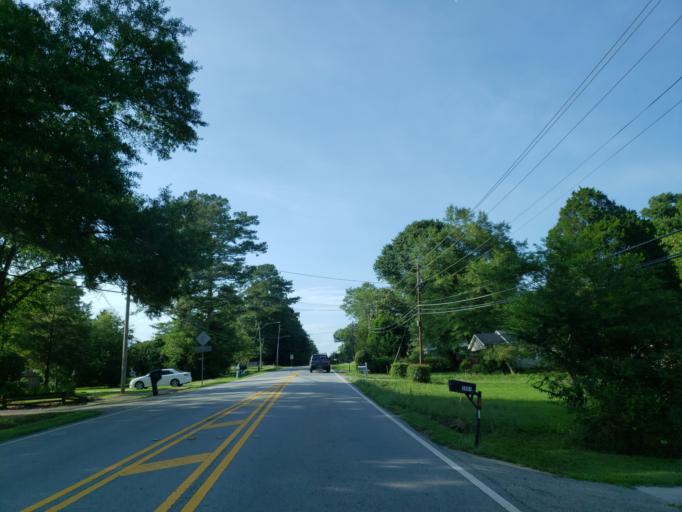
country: US
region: Georgia
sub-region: Cobb County
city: Powder Springs
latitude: 33.8830
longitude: -84.6764
